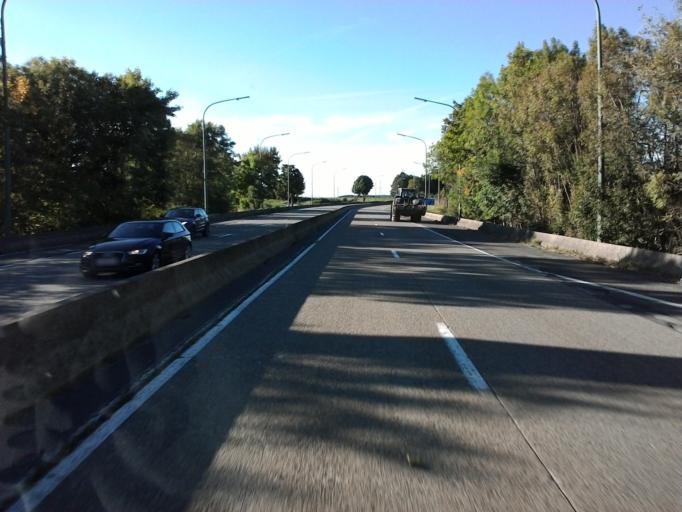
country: BE
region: Wallonia
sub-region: Province du Luxembourg
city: Martelange
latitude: 49.8654
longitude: 5.7159
